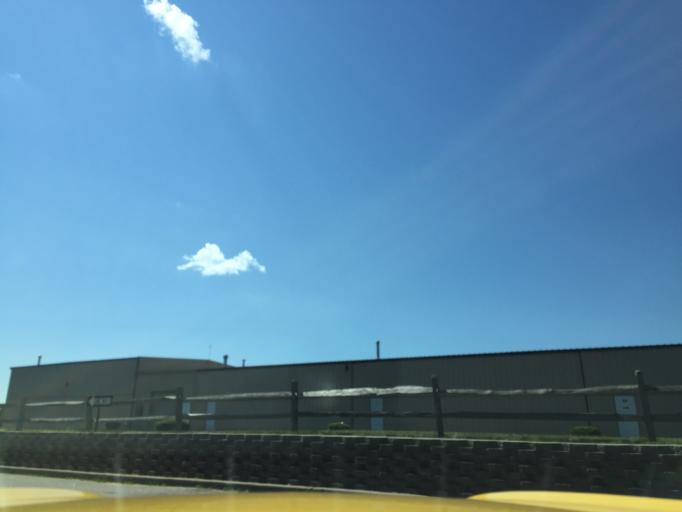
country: US
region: New York
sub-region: Suffolk County
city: Northwest Harbor
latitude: 40.9613
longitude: -72.2475
